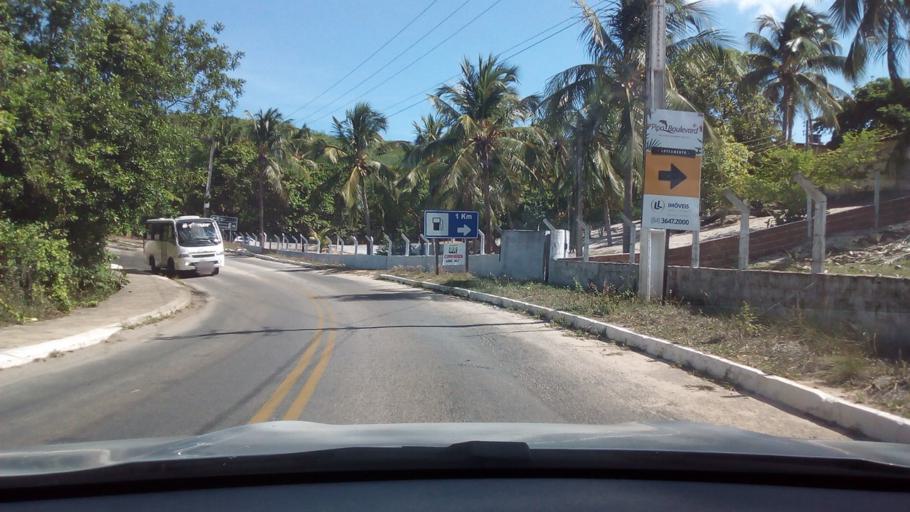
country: BR
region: Rio Grande do Norte
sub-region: Ares
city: Ares
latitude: -6.2275
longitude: -35.0678
